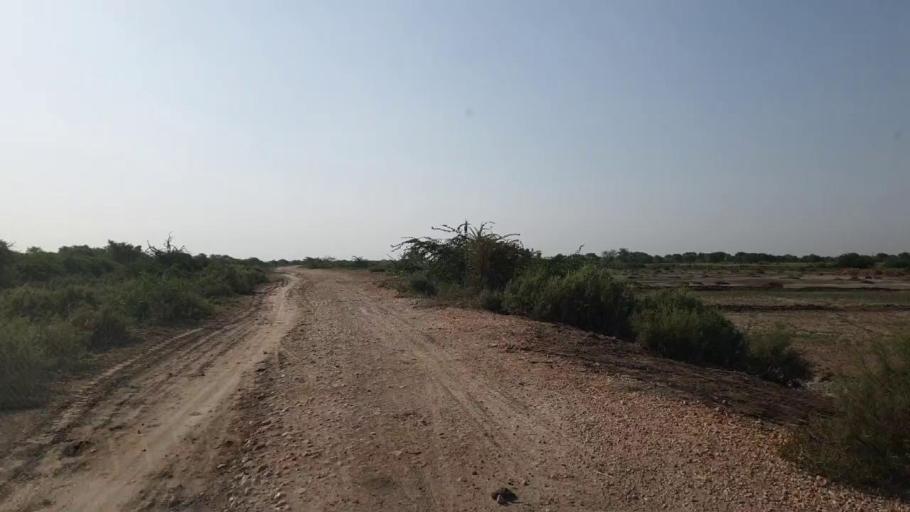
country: PK
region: Sindh
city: Kadhan
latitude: 24.6220
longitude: 69.0728
